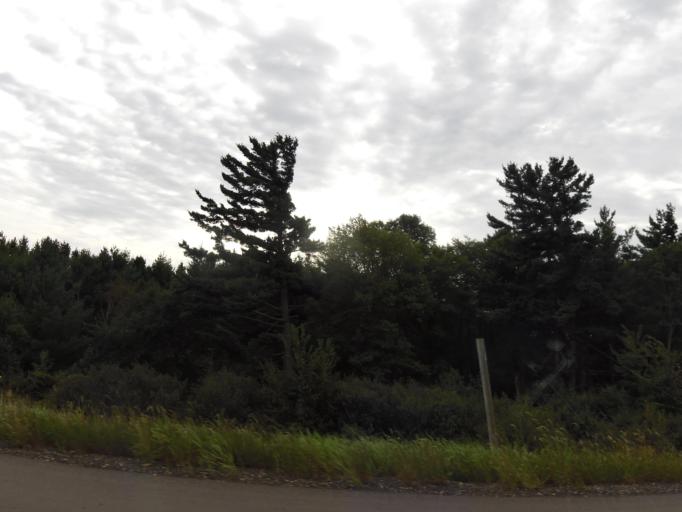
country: US
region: Wisconsin
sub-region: Monroe County
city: Tomah
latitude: 43.9769
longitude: -90.4635
